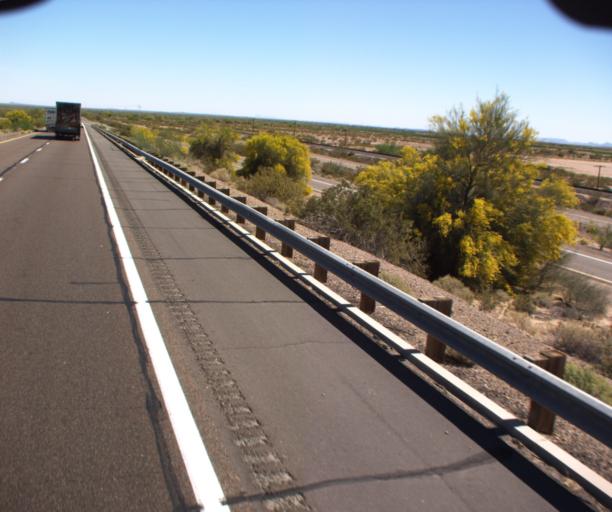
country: US
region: Arizona
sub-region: Yuma County
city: Wellton
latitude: 32.8246
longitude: -113.4409
